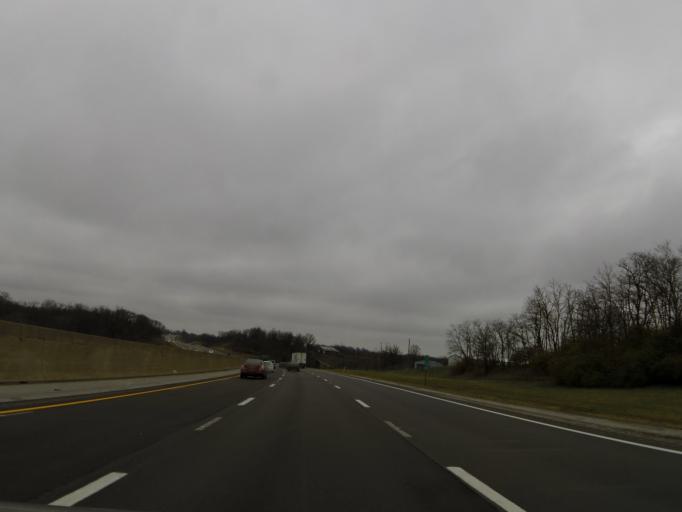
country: US
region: Kentucky
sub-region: Grant County
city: Dry Ridge
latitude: 38.6756
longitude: -84.6010
